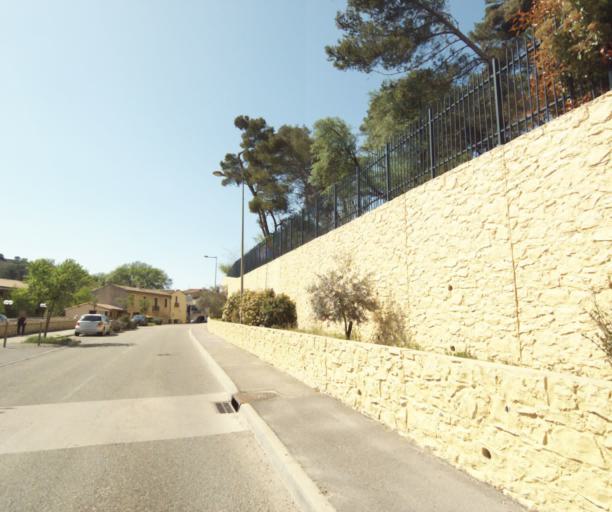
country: FR
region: Languedoc-Roussillon
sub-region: Departement de l'Herault
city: Grabels
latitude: 43.6499
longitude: 3.7928
